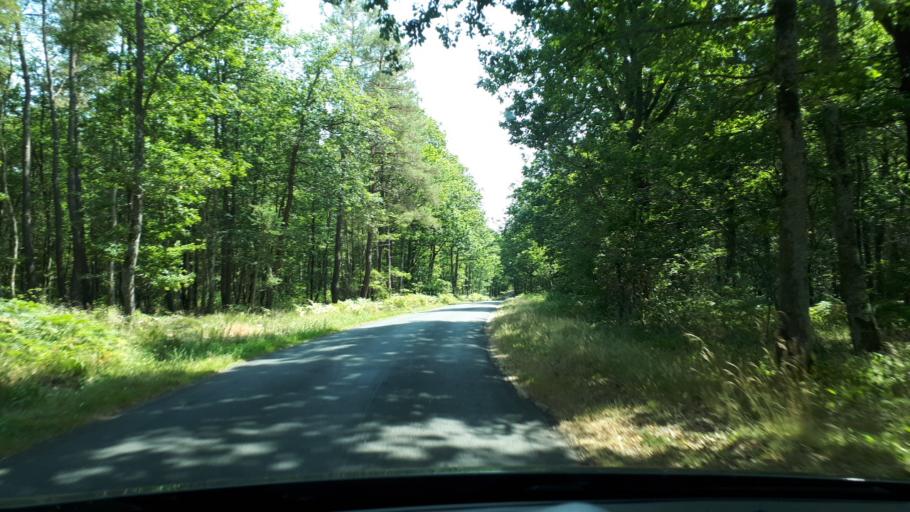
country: FR
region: Centre
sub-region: Departement du Loir-et-Cher
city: Naveil
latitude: 47.8294
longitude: 1.0395
